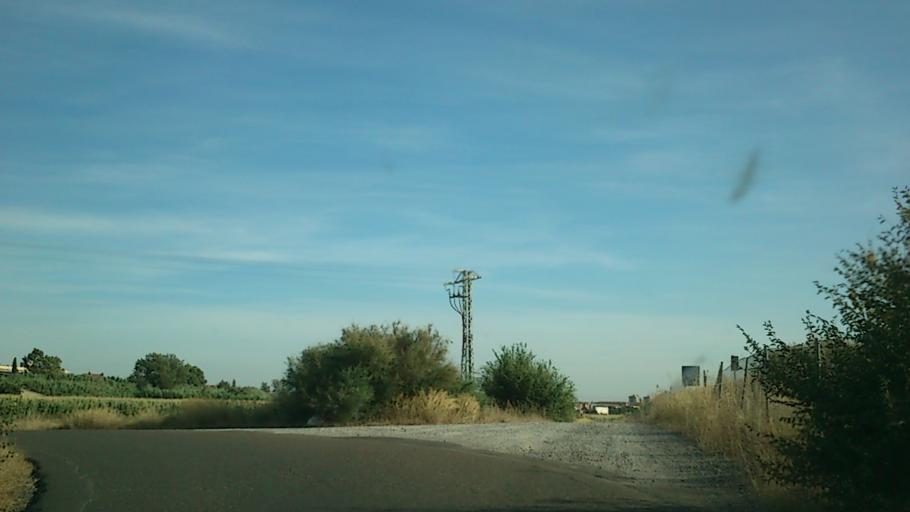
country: ES
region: Aragon
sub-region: Provincia de Zaragoza
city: Zaragoza
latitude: 41.6889
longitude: -0.8326
